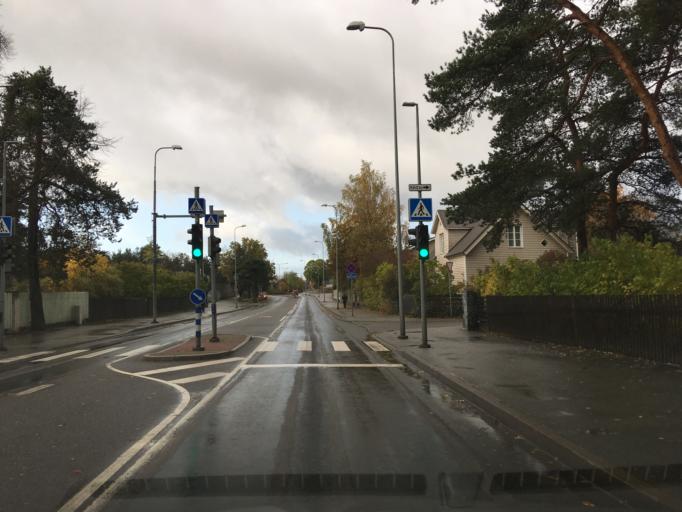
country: EE
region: Harju
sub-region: Saue vald
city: Laagri
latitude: 59.3705
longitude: 24.6396
